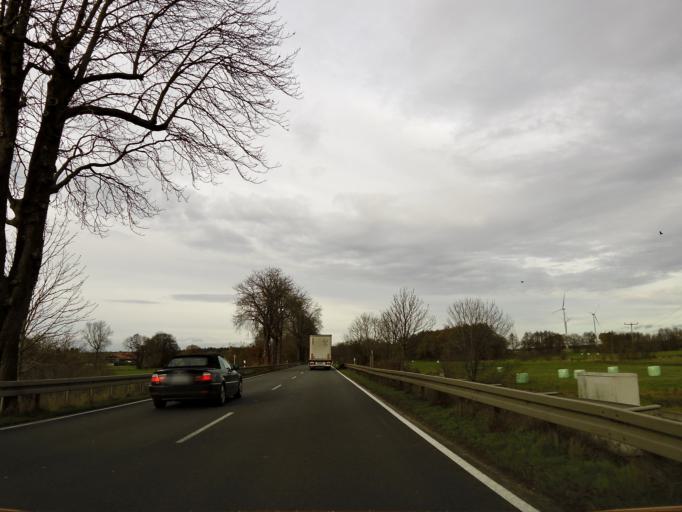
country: DE
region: Saxony-Anhalt
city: Klotze
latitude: 52.6970
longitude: 11.2590
